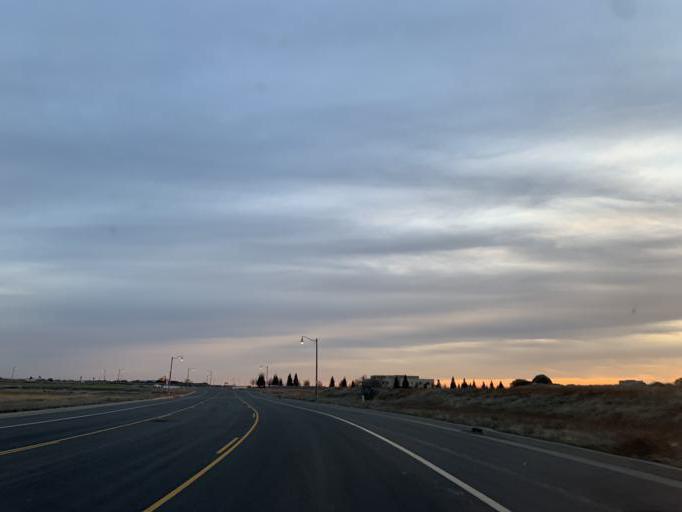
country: US
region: California
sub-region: Placer County
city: Lincoln
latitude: 38.8595
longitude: -121.2945
